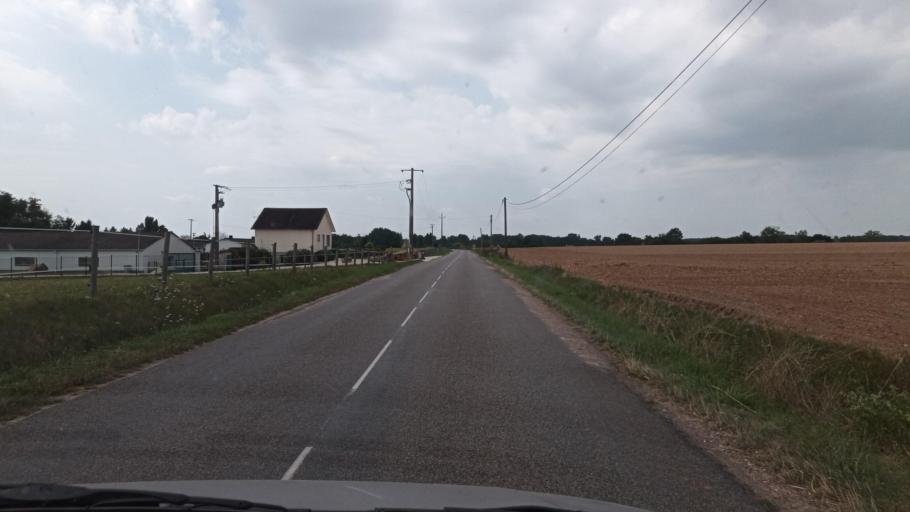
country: FR
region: Bourgogne
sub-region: Departement de l'Yonne
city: Egriselles-le-Bocage
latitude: 48.0291
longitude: 3.1831
